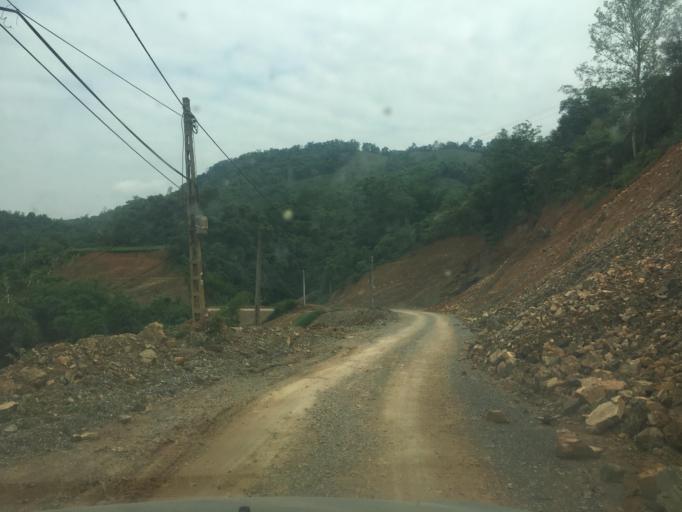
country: VN
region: Lang Son
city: Binh Gia
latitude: 22.1333
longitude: 106.3400
